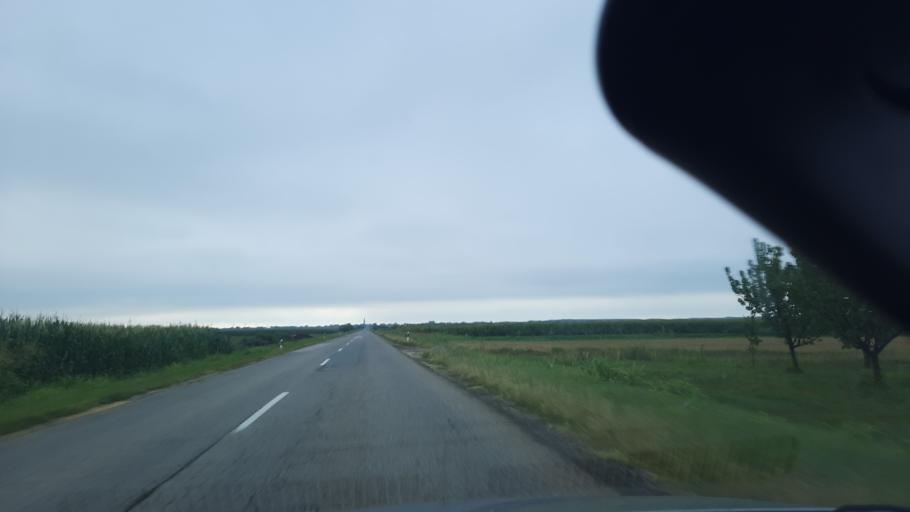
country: RS
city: Farkazdin
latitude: 45.1969
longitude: 20.4484
